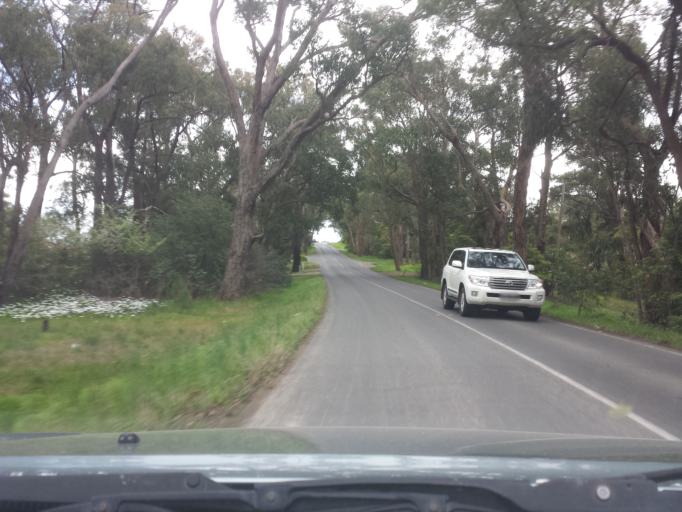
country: AU
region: Victoria
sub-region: Yarra Ranges
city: Mount Evelyn
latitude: -37.7639
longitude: 145.3748
